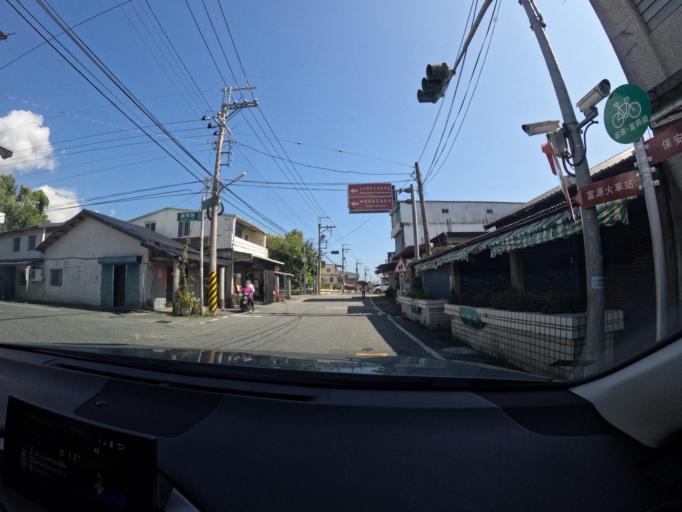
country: TW
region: Taiwan
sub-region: Hualien
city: Hualian
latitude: 23.5770
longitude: 121.3762
